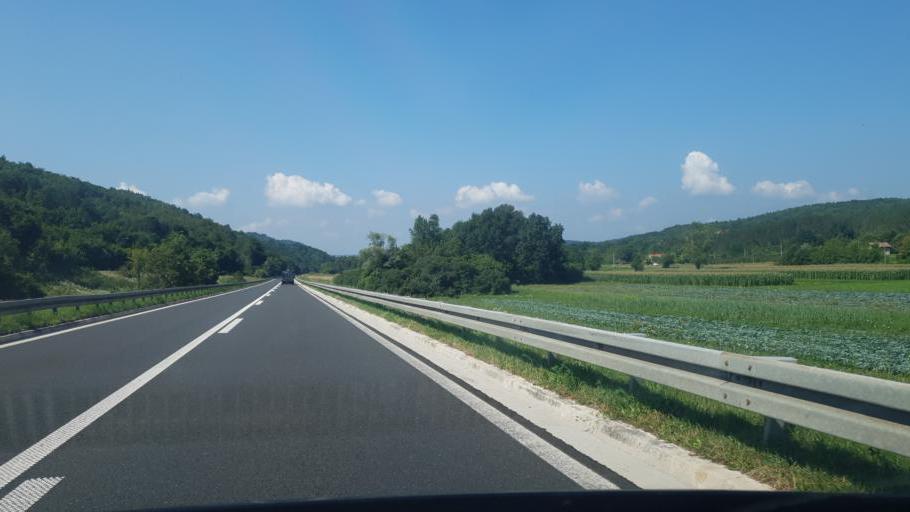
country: HR
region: Istarska
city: Pazin
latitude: 45.2995
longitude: 14.0488
